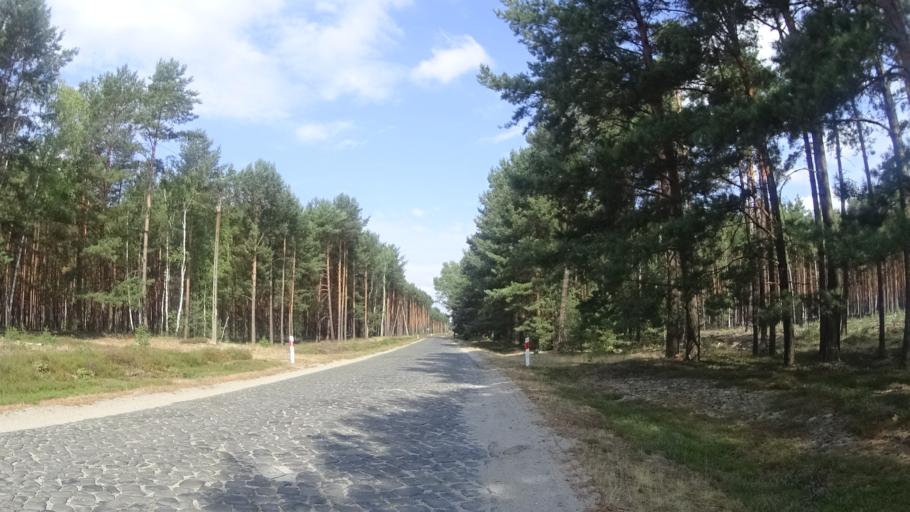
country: PL
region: Lubusz
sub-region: Powiat zarski
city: Leknica
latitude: 51.5121
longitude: 14.8346
